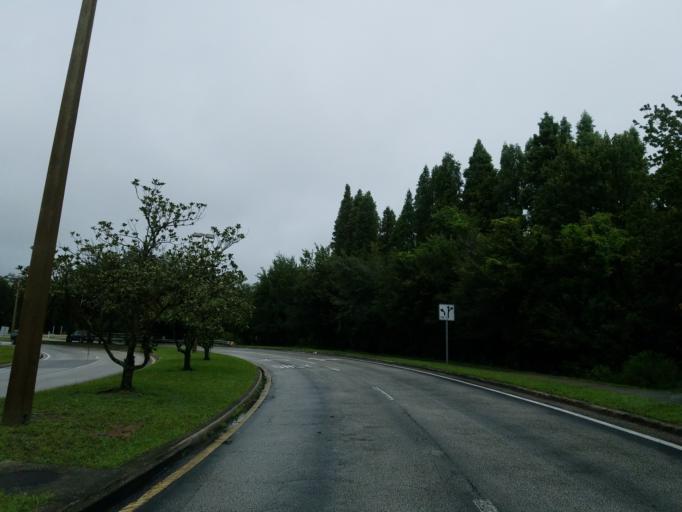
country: US
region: Florida
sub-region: Hillsborough County
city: Brandon
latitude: 27.9297
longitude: -82.3204
